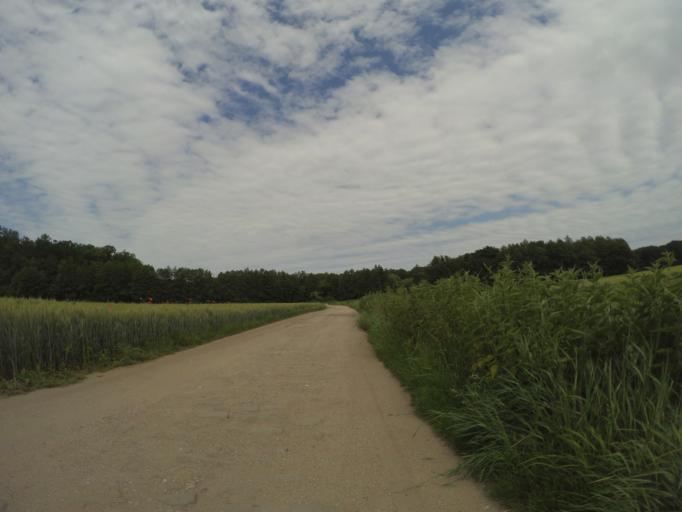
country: CZ
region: Central Bohemia
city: Celakovice
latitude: 50.1757
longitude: 14.7847
